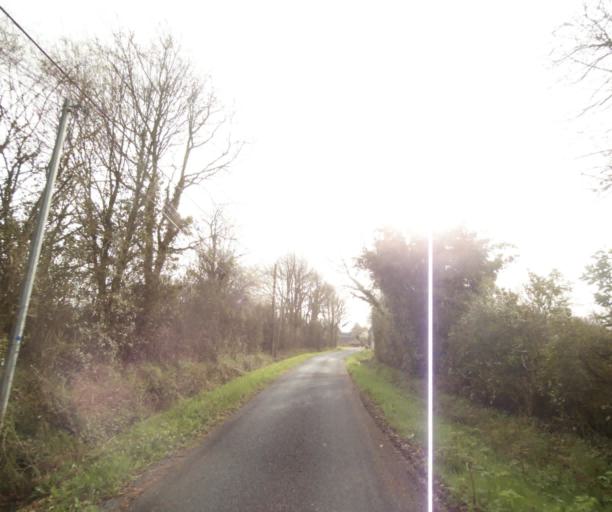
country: FR
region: Pays de la Loire
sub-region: Departement de la Loire-Atlantique
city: Bouvron
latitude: 47.4014
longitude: -1.8826
